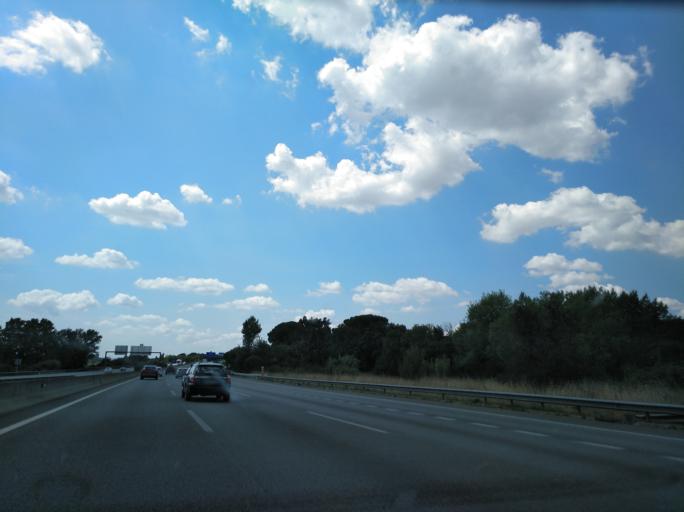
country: ES
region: Catalonia
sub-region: Provincia de Barcelona
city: La Roca del Valles
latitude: 41.6070
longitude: 2.3430
